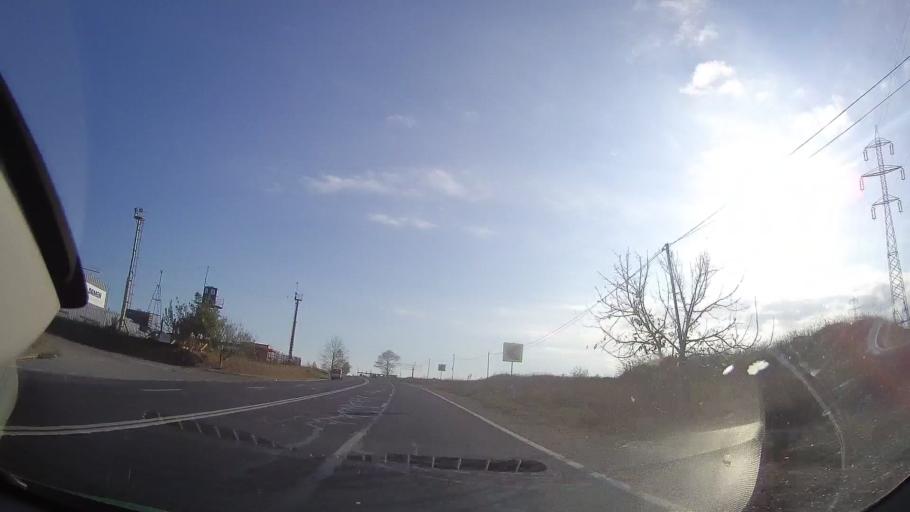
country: RO
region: Constanta
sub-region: Municipiul Mangalia
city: Mangalia
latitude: 43.7985
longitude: 28.5592
